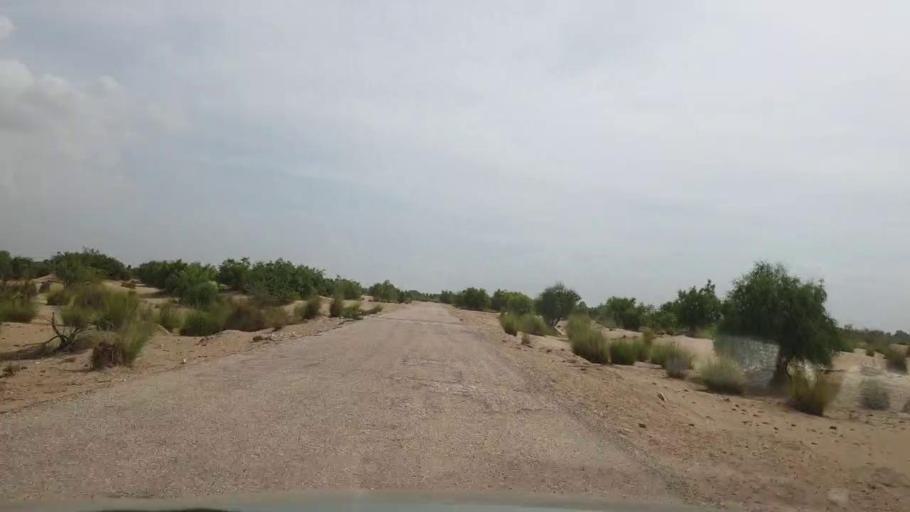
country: PK
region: Sindh
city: Bozdar
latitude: 27.0954
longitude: 69.0165
